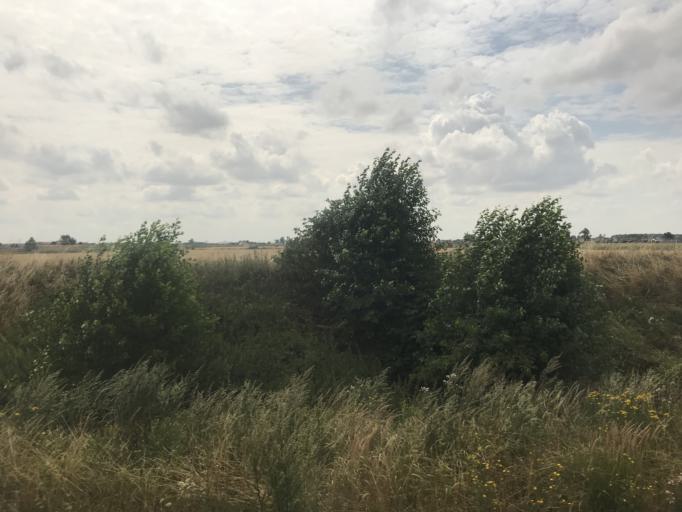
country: PL
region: Greater Poland Voivodeship
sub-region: Powiat gnieznienski
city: Gniezno
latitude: 52.5162
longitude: 17.5371
